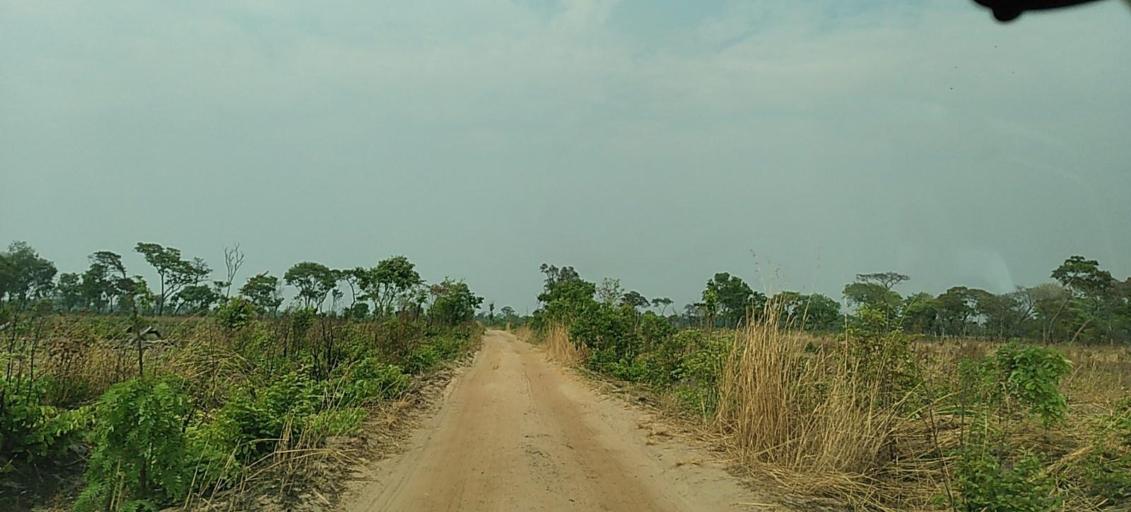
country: ZM
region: North-Western
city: Kabompo
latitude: -13.4864
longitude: 24.4123
